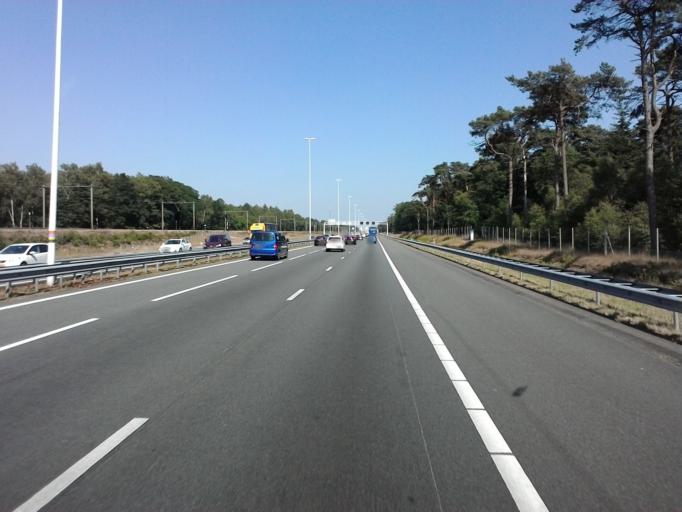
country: NL
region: Utrecht
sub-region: Gemeente Utrechtse Heuvelrug
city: Driebergen-Rijsenburg
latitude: 52.0650
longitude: 5.2883
